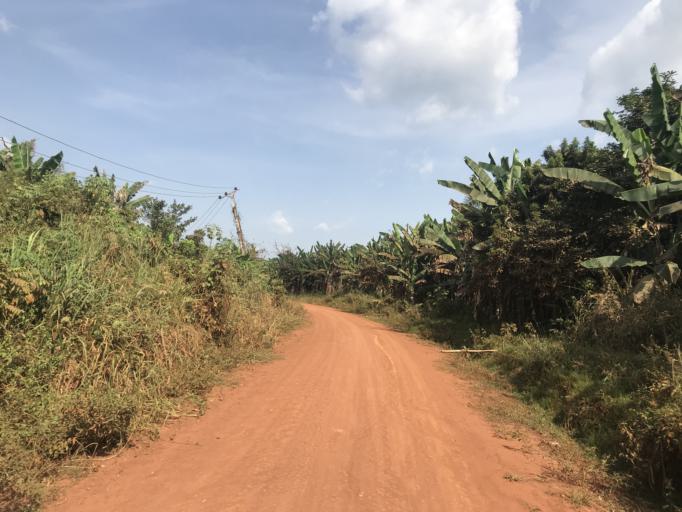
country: NG
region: Osun
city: Ilesa
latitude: 7.6559
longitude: 4.6699
